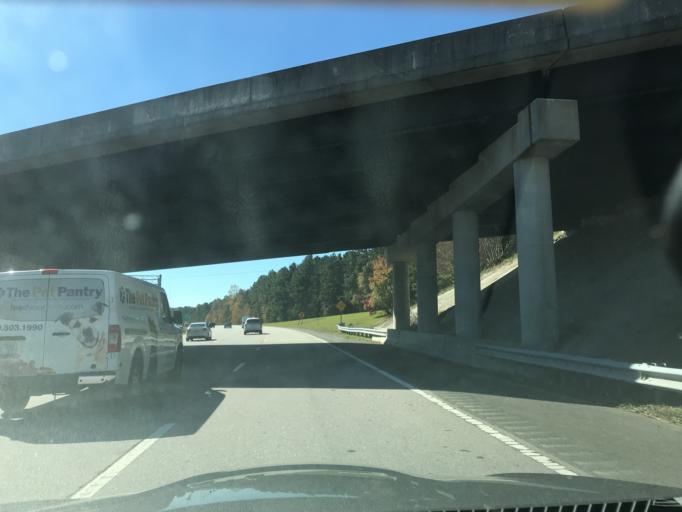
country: US
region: North Carolina
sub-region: Durham County
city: Durham
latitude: 36.0124
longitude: -78.9552
